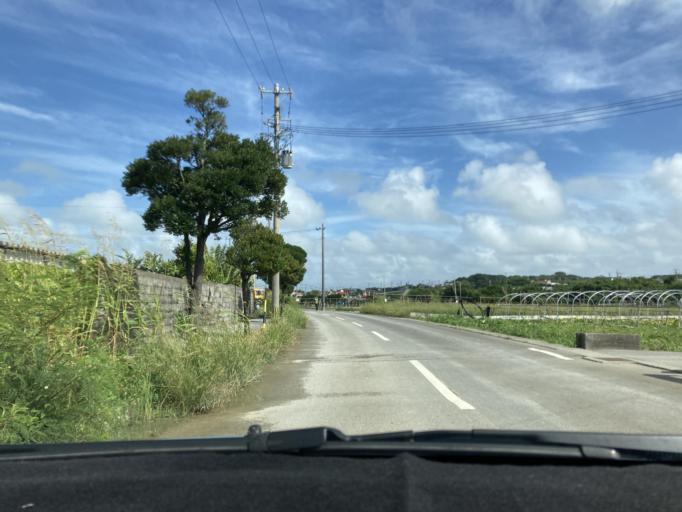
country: JP
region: Okinawa
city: Itoman
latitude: 26.0995
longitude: 127.6614
